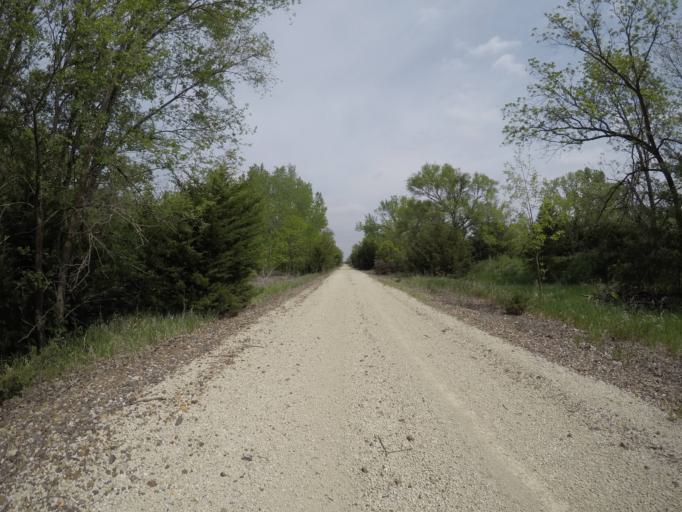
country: US
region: Nebraska
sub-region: Gage County
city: Wymore
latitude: 40.2030
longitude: -96.6606
